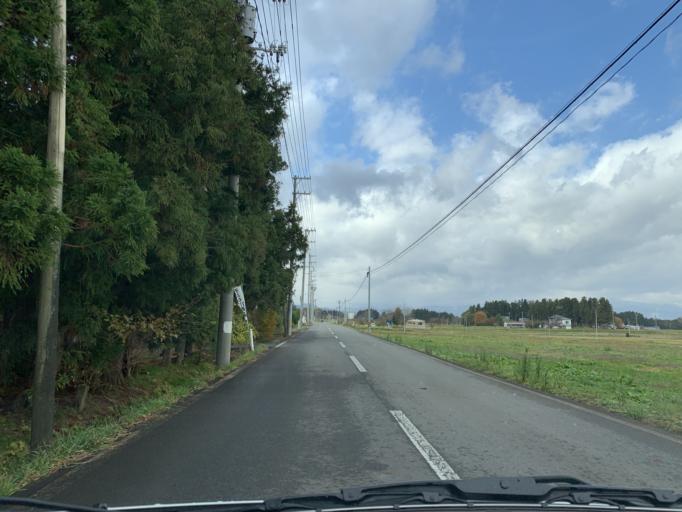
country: JP
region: Iwate
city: Mizusawa
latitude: 39.0638
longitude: 141.0954
